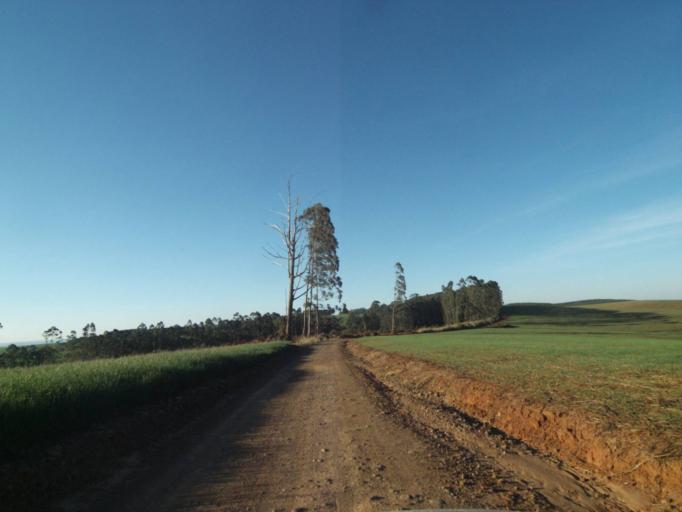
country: BR
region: Parana
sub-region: Telemaco Borba
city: Telemaco Borba
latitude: -24.4815
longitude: -50.5935
